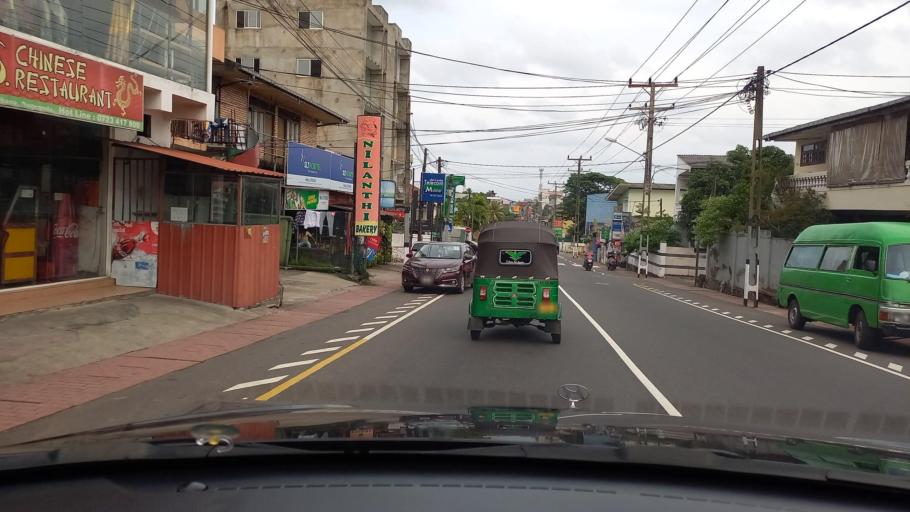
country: LK
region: Western
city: Sri Jayewardenepura Kotte
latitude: 6.8714
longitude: 79.9058
